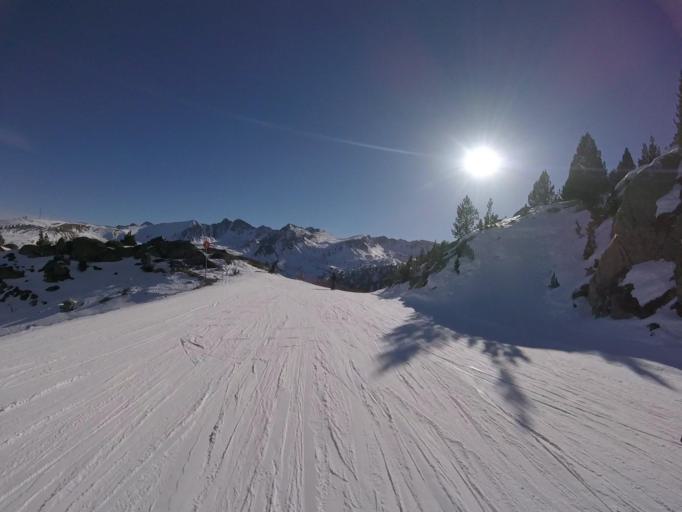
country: AD
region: Encamp
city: Pas de la Casa
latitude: 42.5301
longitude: 1.6851
